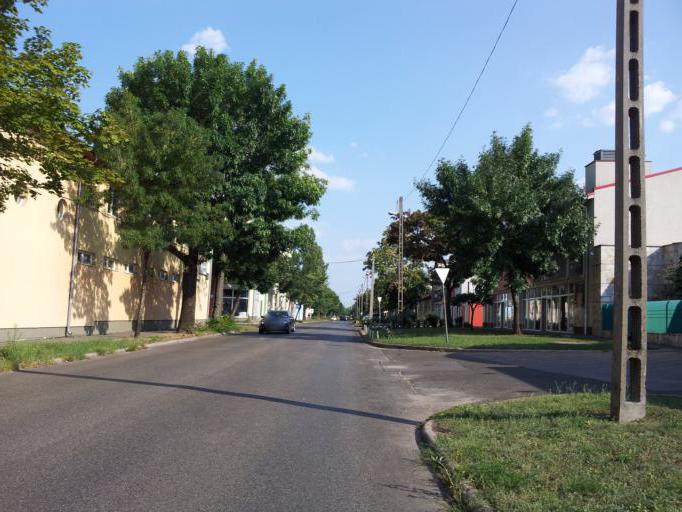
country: HU
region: Budapest
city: Budapest X. keruelet
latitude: 47.4812
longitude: 19.1216
